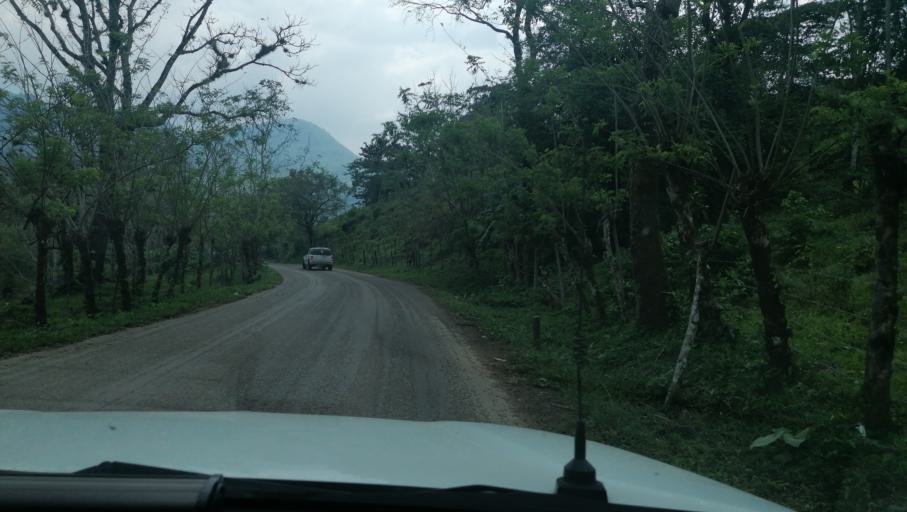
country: MX
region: Chiapas
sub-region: Francisco Leon
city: San Miguel la Sardina
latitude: 17.2265
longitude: -93.3451
